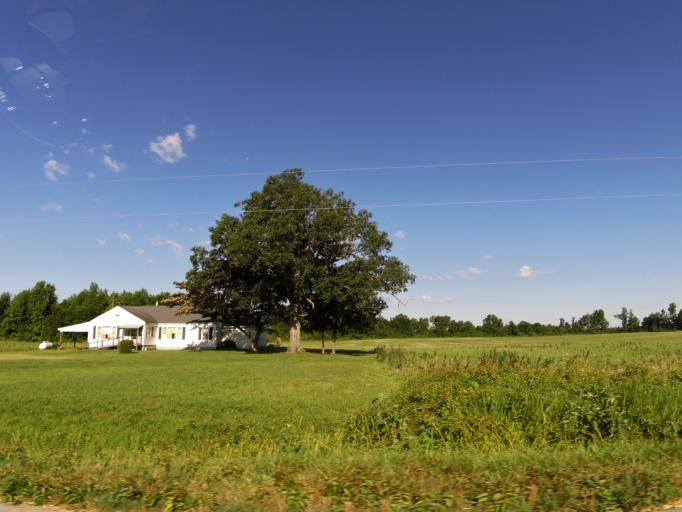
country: US
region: Missouri
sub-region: Butler County
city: Poplar Bluff
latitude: 36.6113
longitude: -90.5204
